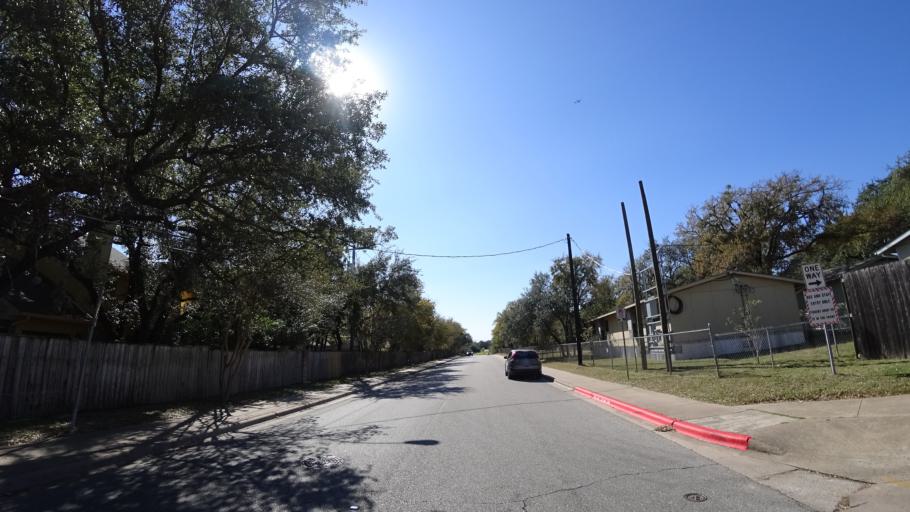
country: US
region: Texas
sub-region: Williamson County
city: Jollyville
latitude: 30.3764
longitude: -97.7475
